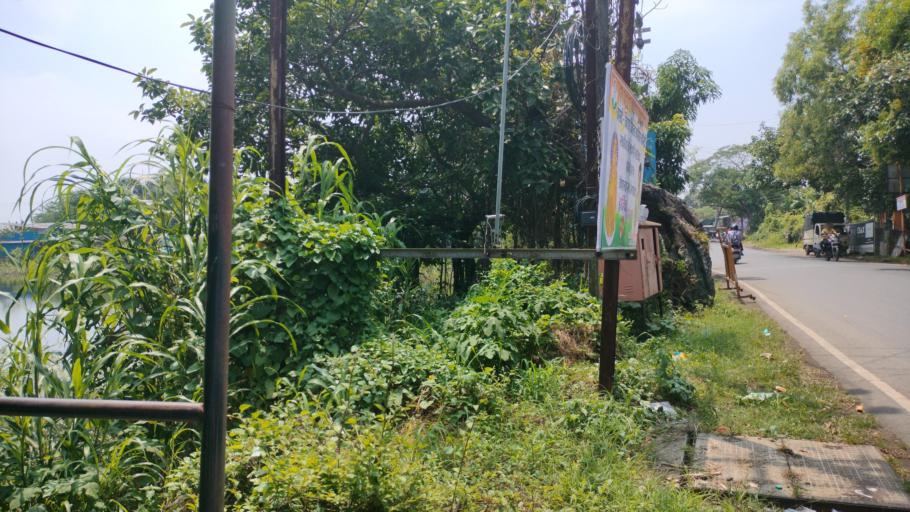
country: IN
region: Maharashtra
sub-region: Thane
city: Virar
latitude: 19.3915
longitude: 72.7822
